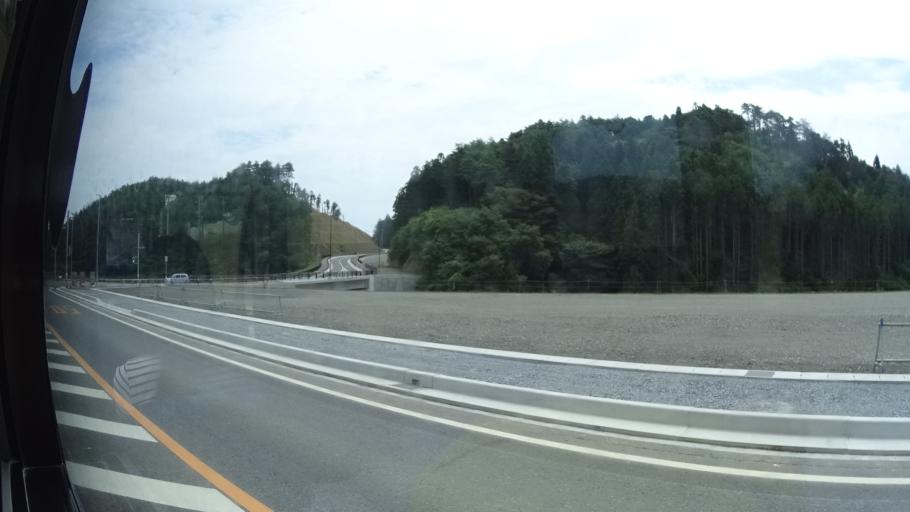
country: JP
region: Miyagi
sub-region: Oshika Gun
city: Onagawa Cho
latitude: 38.6849
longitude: 141.4533
